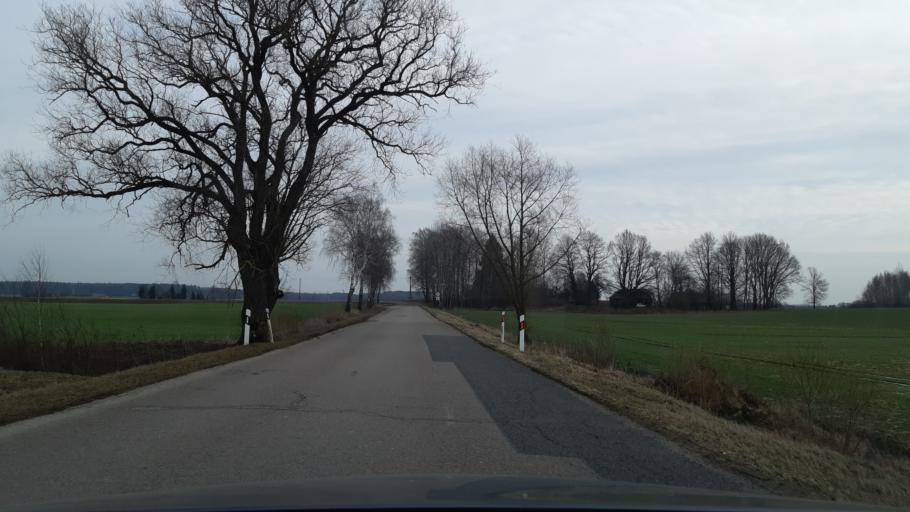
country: LT
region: Marijampoles apskritis
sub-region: Marijampole Municipality
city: Marijampole
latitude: 54.7175
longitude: 23.3279
